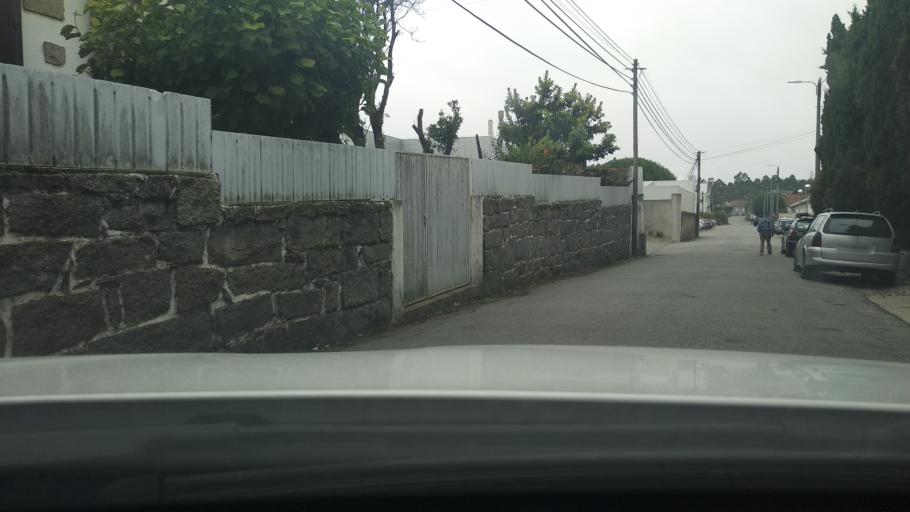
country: PT
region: Aveiro
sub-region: Espinho
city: Souto
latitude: 40.9849
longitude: -8.6193
